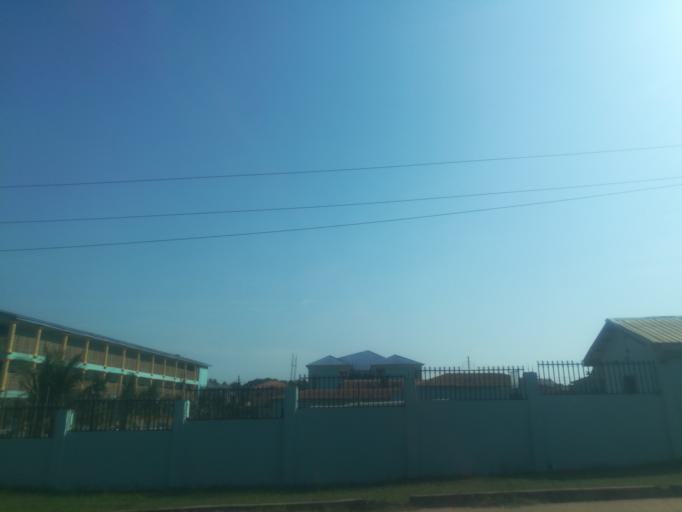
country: NG
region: Ogun
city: Abeokuta
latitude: 7.1366
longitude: 3.2954
